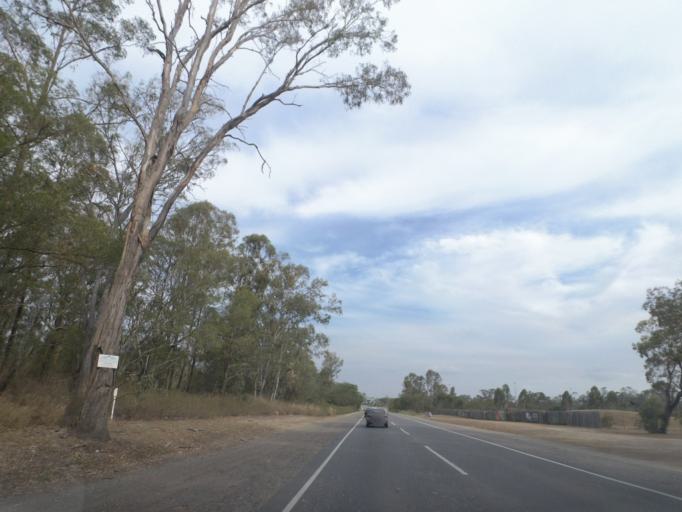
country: AU
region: Queensland
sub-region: Brisbane
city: Inala
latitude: -27.5957
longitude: 153.0081
